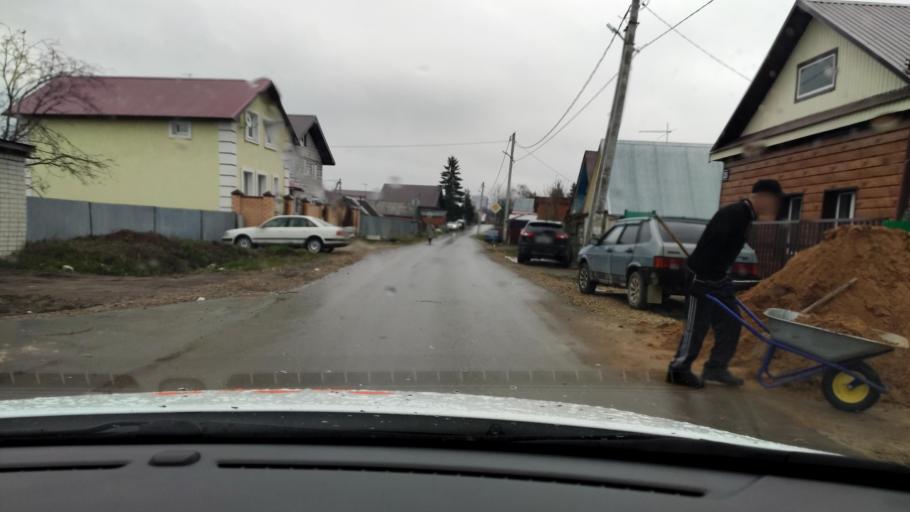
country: RU
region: Tatarstan
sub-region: Gorod Kazan'
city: Kazan
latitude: 55.7252
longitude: 49.1431
